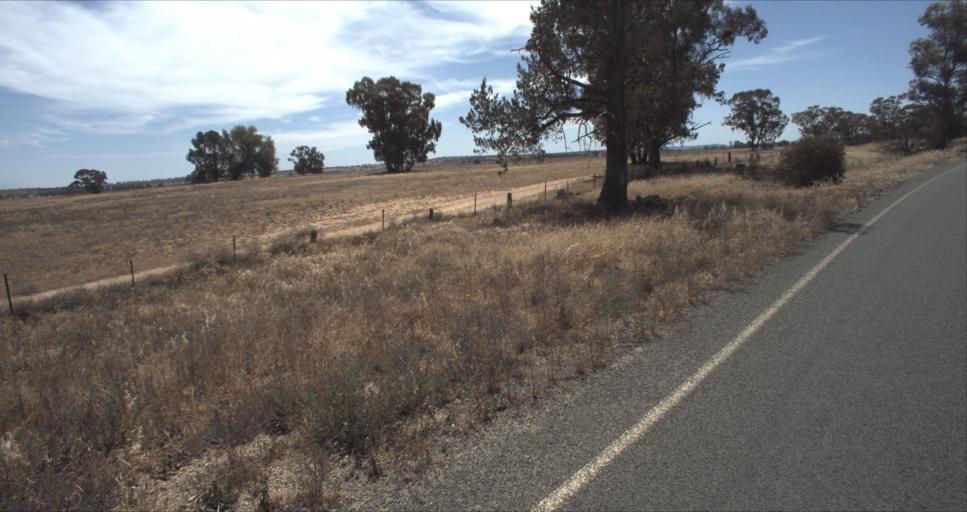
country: AU
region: New South Wales
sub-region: Leeton
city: Leeton
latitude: -34.6538
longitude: 146.4614
